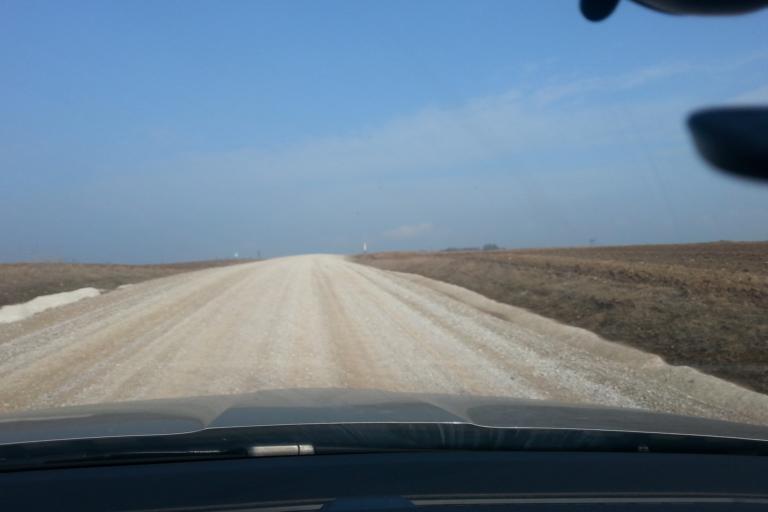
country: LT
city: Trakai
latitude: 54.5973
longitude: 24.9782
